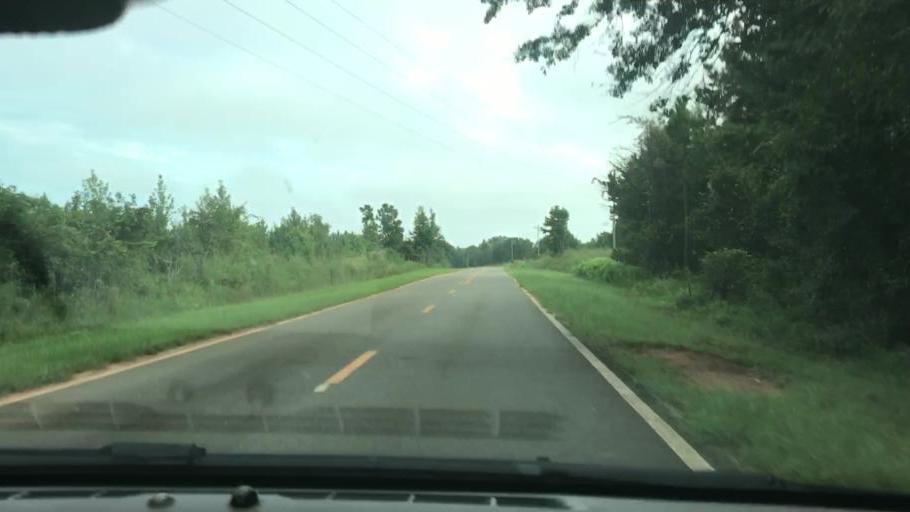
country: US
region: Georgia
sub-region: Stewart County
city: Lumpkin
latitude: 32.0355
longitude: -84.9102
